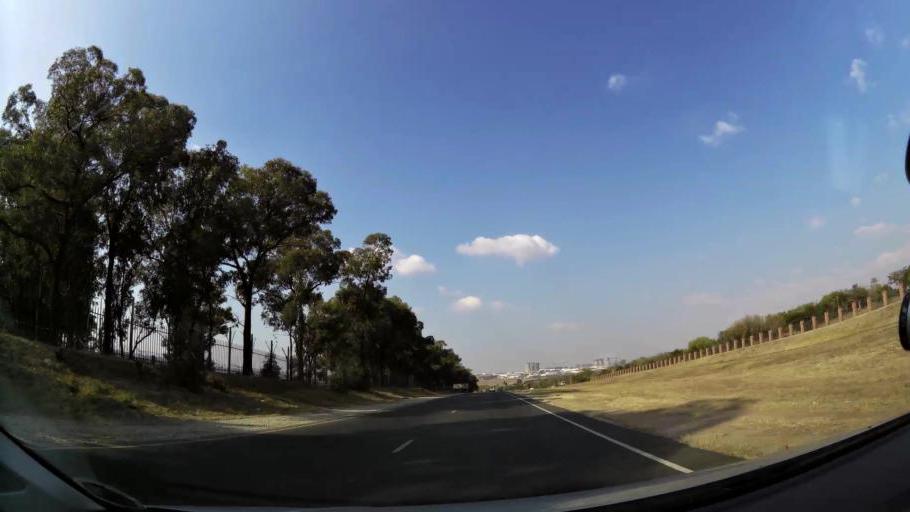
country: ZA
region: Gauteng
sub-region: City of Johannesburg Metropolitan Municipality
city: Modderfontein
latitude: -26.1097
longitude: 28.1569
